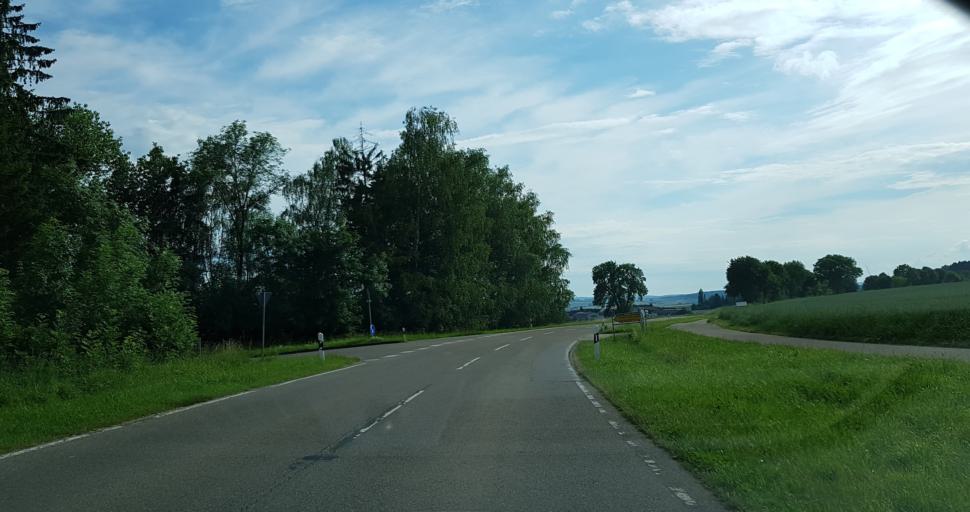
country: DE
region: Baden-Wuerttemberg
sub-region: Tuebingen Region
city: Altheim
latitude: 48.3174
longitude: 9.7732
